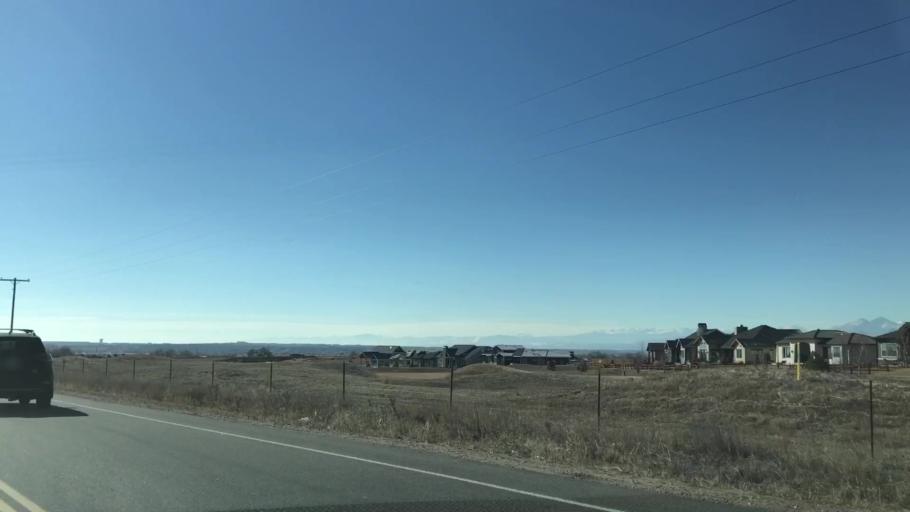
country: US
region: Colorado
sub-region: Weld County
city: Windsor
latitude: 40.5299
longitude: -104.9443
